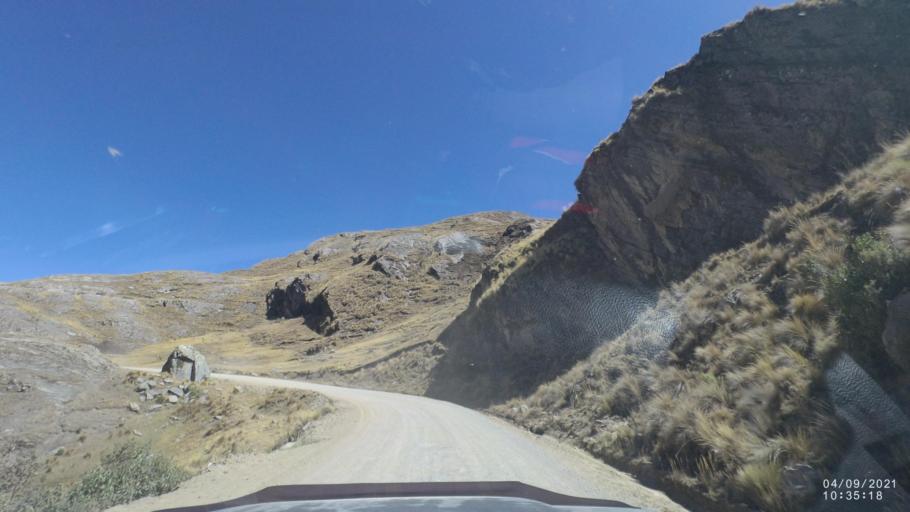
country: BO
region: Cochabamba
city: Sipe Sipe
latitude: -17.2899
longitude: -66.4467
